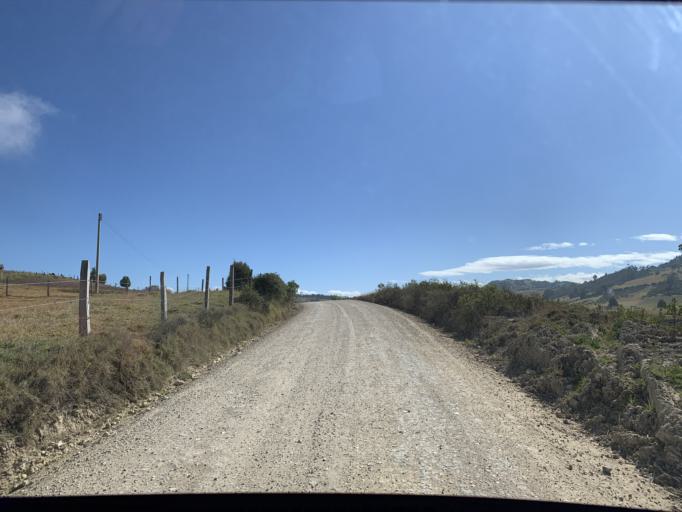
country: CO
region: Boyaca
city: Tuta
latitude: 5.6741
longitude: -73.1478
